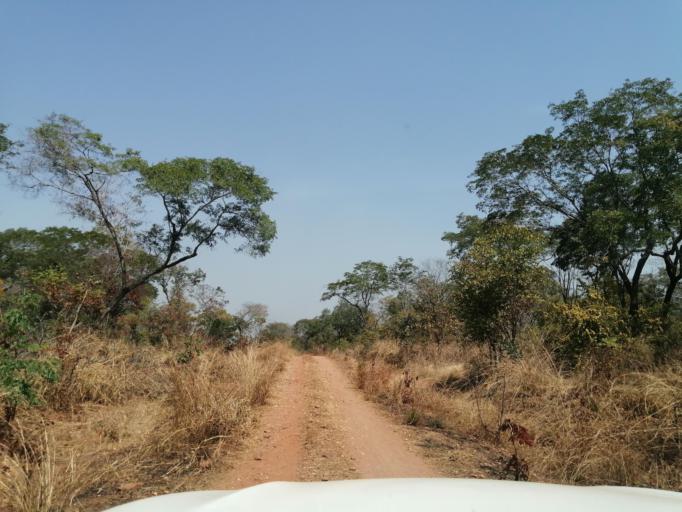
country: ZM
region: Eastern
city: Nyimba
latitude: -14.3736
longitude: 30.0004
